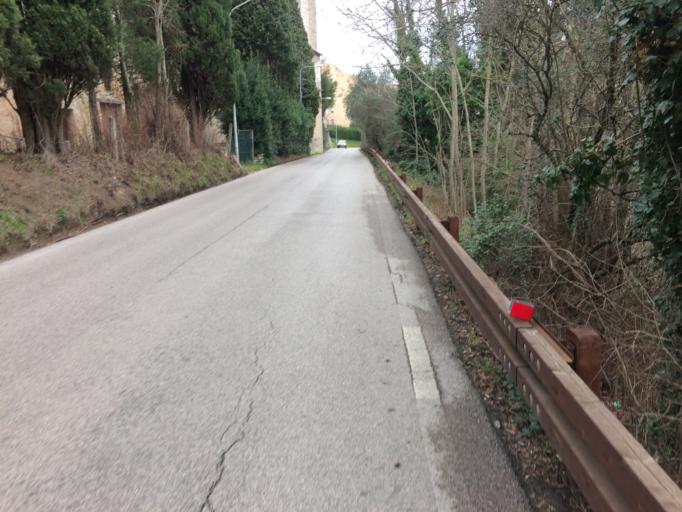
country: IT
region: Umbria
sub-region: Provincia di Perugia
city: Perugia
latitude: 43.1009
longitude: 12.3965
